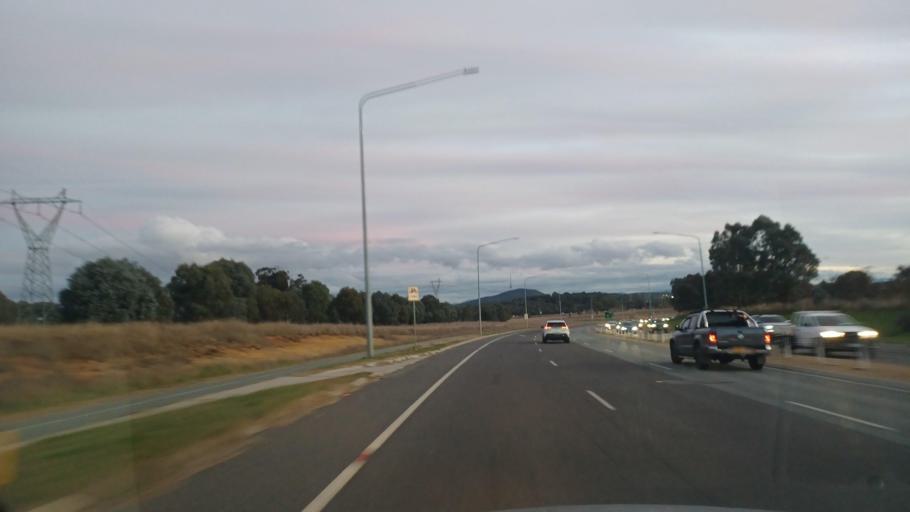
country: AU
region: Australian Capital Territory
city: Kaleen
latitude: -35.2209
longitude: 149.1310
